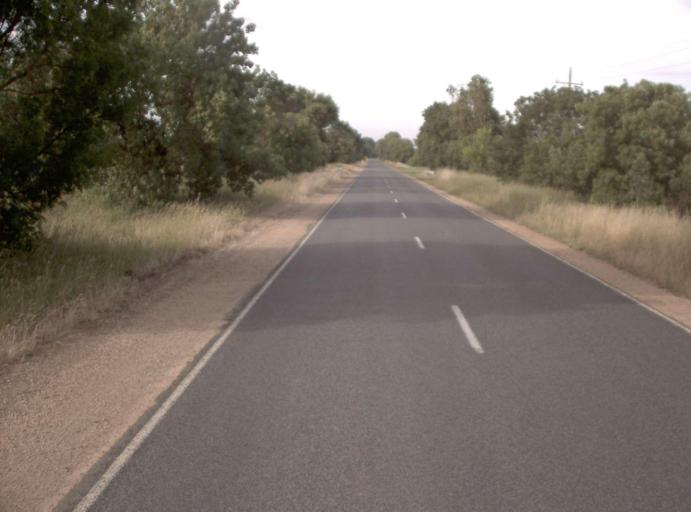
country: AU
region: Victoria
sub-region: Wellington
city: Heyfield
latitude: -37.9724
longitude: 146.8898
